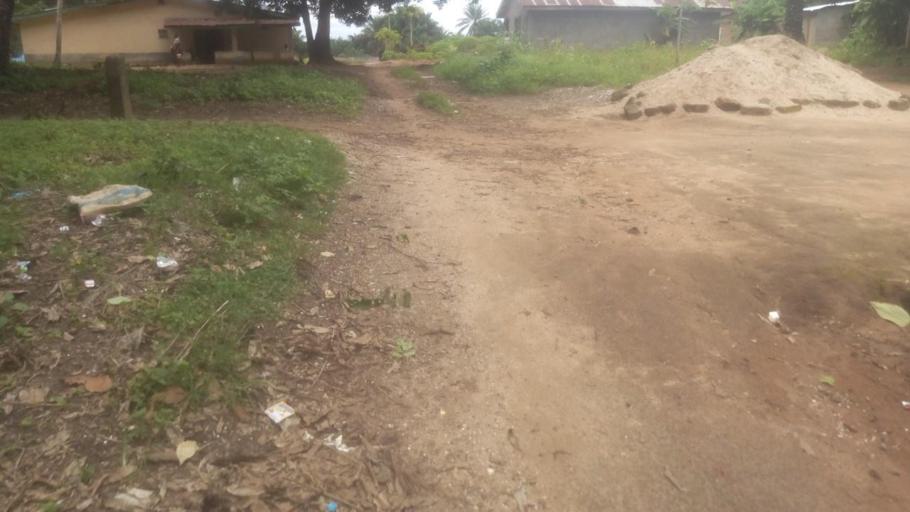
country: SL
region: Northern Province
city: Masoyila
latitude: 8.5572
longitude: -13.1651
